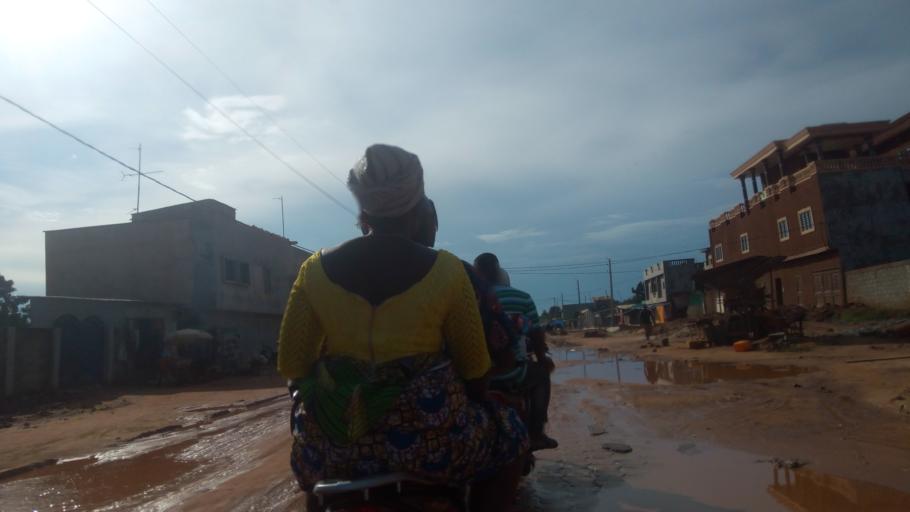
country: BJ
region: Atlantique
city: Abomey-Calavi
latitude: 6.4532
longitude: 2.3368
